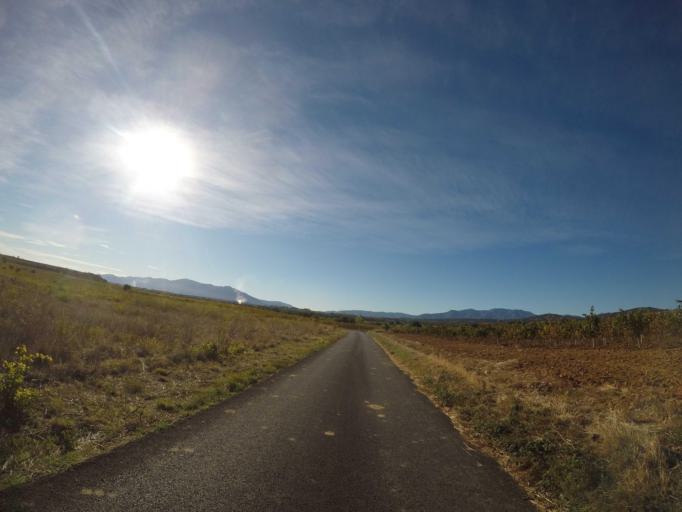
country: FR
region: Languedoc-Roussillon
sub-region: Departement des Pyrenees-Orientales
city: Llupia
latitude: 42.5925
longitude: 2.7645
